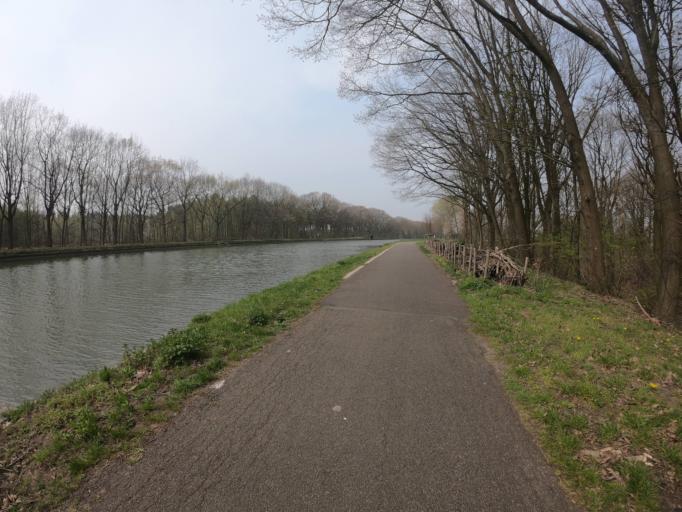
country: BE
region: Flanders
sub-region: Provincie Limburg
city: Maasmechelen
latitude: 51.0276
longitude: 5.7083
